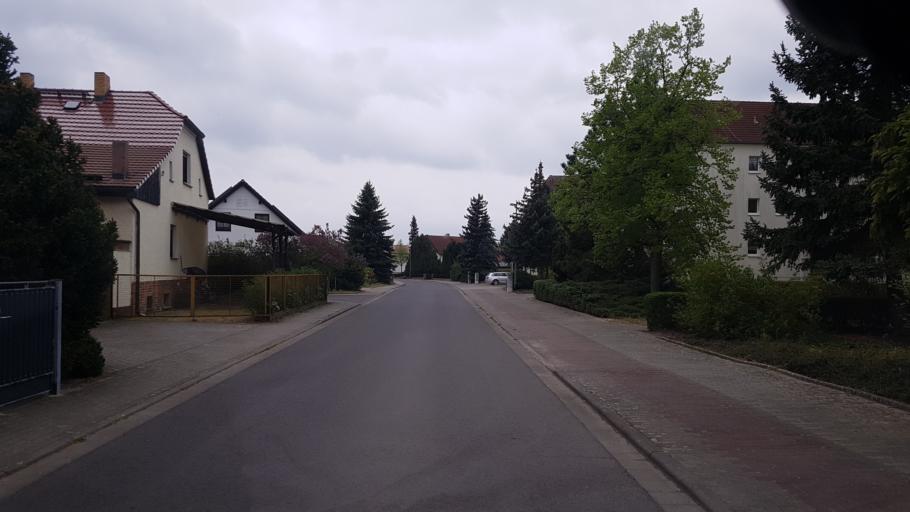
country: DE
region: Brandenburg
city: Altdobern
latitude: 51.6489
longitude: 14.0234
